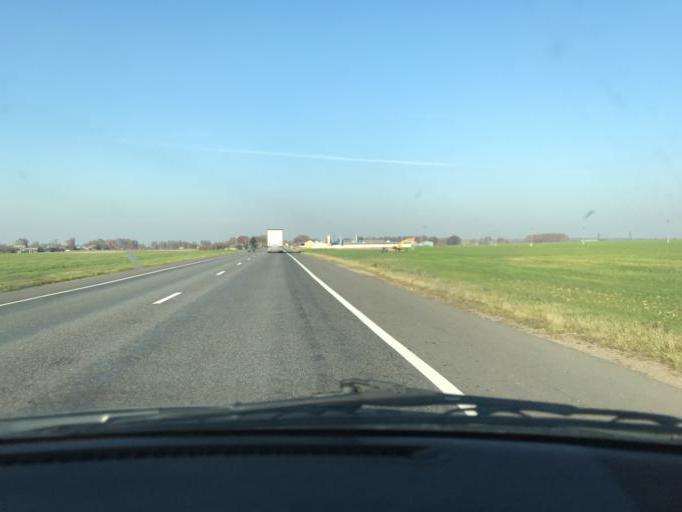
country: BY
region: Mogilev
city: Shklow
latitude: 54.2413
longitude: 30.4512
